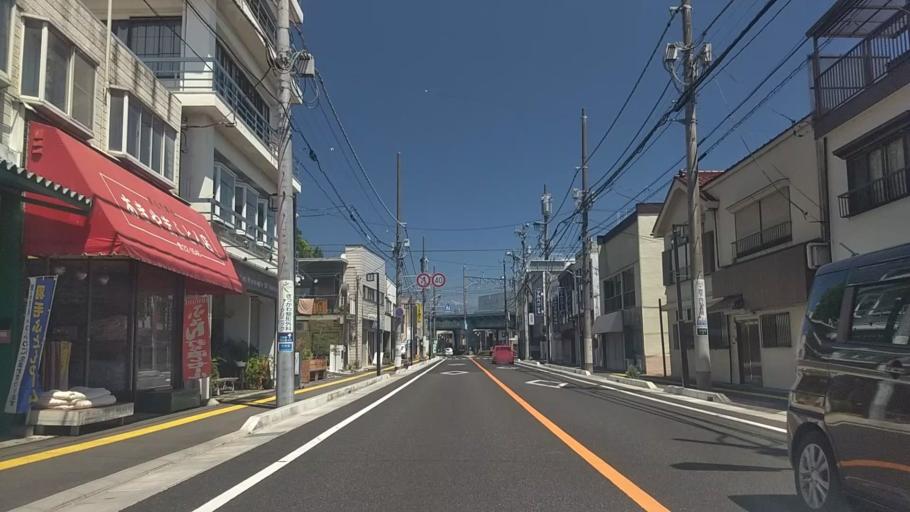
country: JP
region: Yamanashi
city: Nirasaki
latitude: 35.7096
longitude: 138.4501
